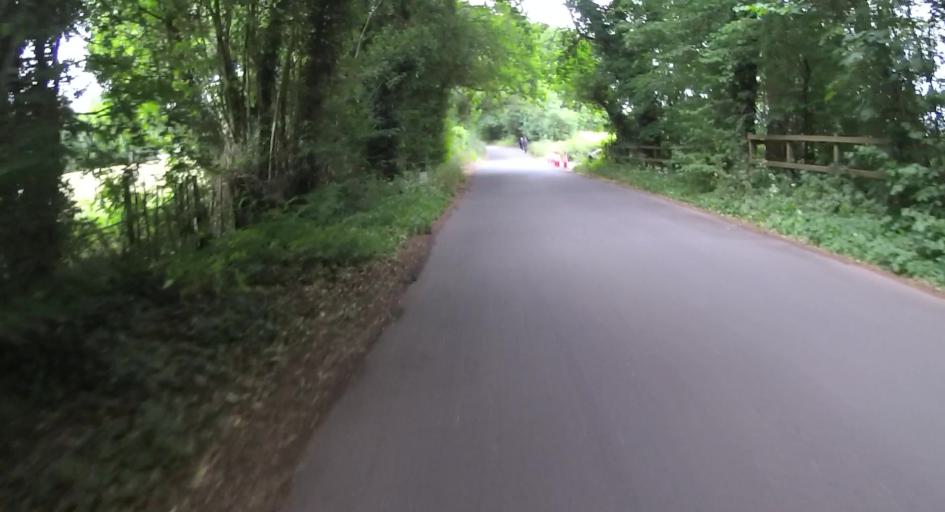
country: GB
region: England
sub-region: Surrey
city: Seale
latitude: 51.2169
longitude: -0.7342
